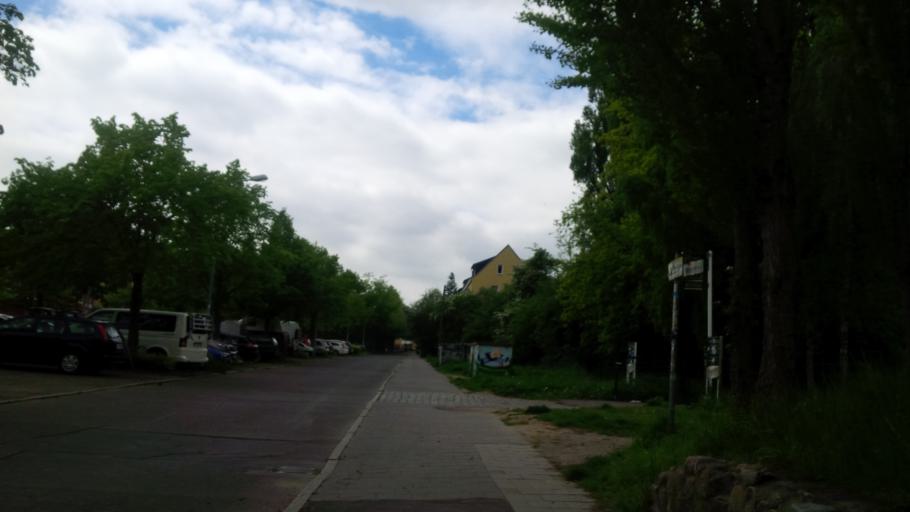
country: DE
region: Mecklenburg-Vorpommern
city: Rostock
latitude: 54.0902
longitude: 12.0970
